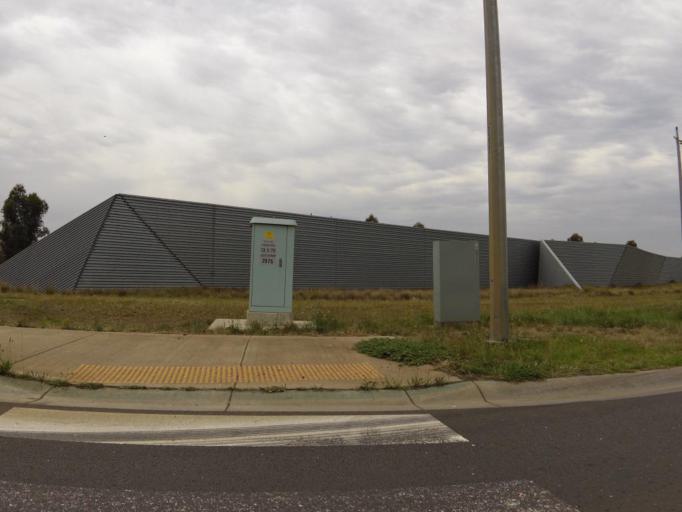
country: AU
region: Victoria
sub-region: Brimbank
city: Derrimut
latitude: -37.7947
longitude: 144.7531
